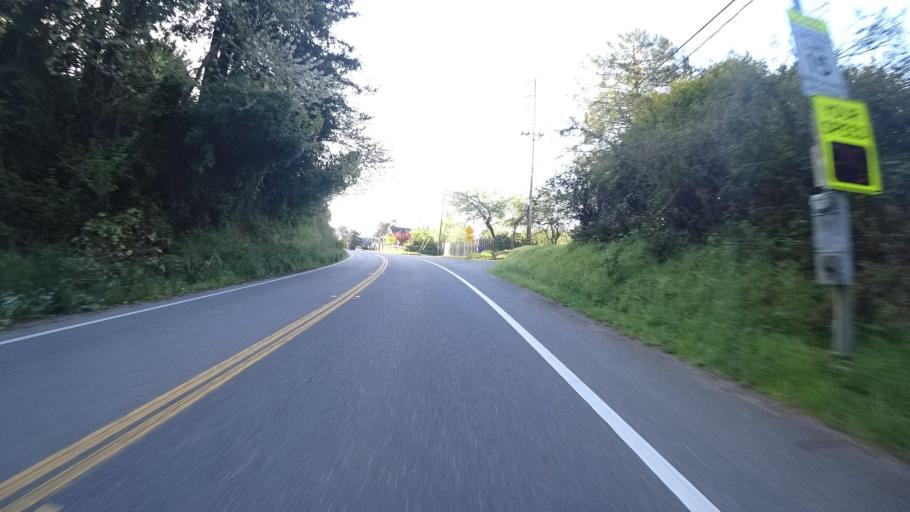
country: US
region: California
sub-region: Humboldt County
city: Myrtletown
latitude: 40.7621
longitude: -124.0624
